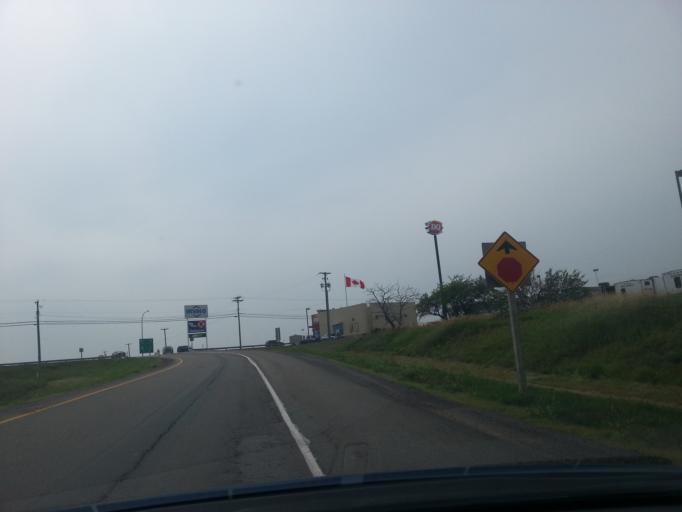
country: CA
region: New Brunswick
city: Salisbury
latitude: 46.0506
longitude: -65.0578
